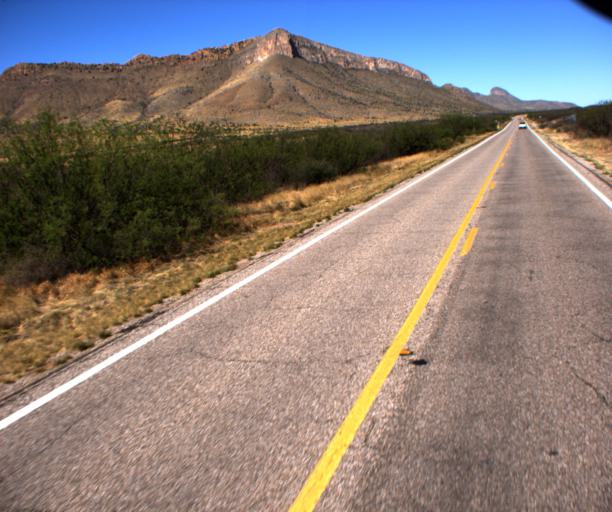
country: US
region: Arizona
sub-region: Cochise County
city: Huachuca City
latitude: 31.6932
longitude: -110.4086
